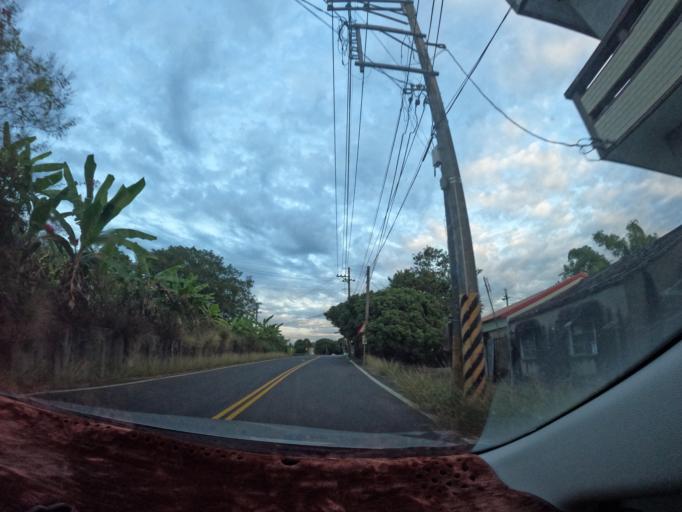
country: TW
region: Taiwan
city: Yujing
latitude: 23.0287
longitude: 120.4149
